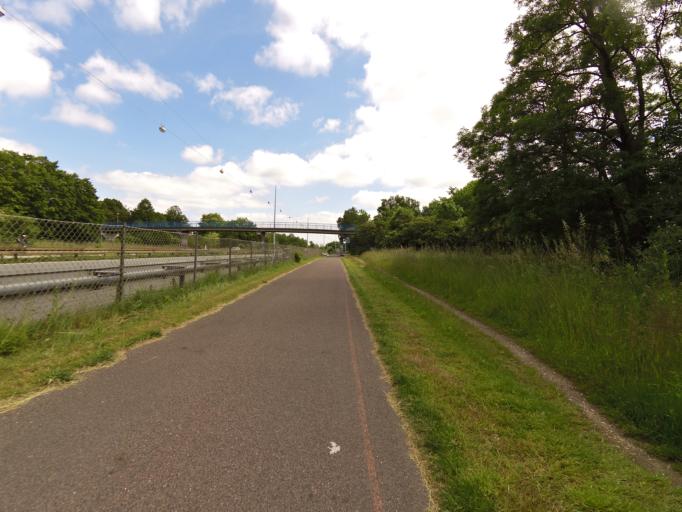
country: DK
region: Capital Region
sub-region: Gladsaxe Municipality
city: Buddinge
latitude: 55.7249
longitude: 12.4864
